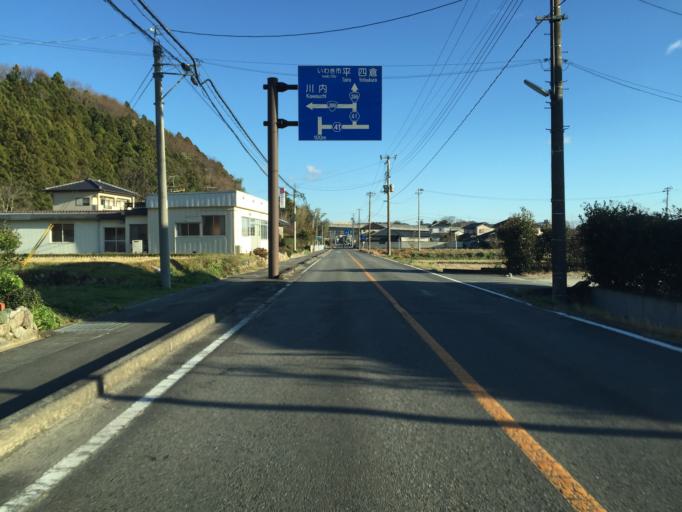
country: JP
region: Fukushima
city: Iwaki
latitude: 37.1373
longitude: 140.8510
